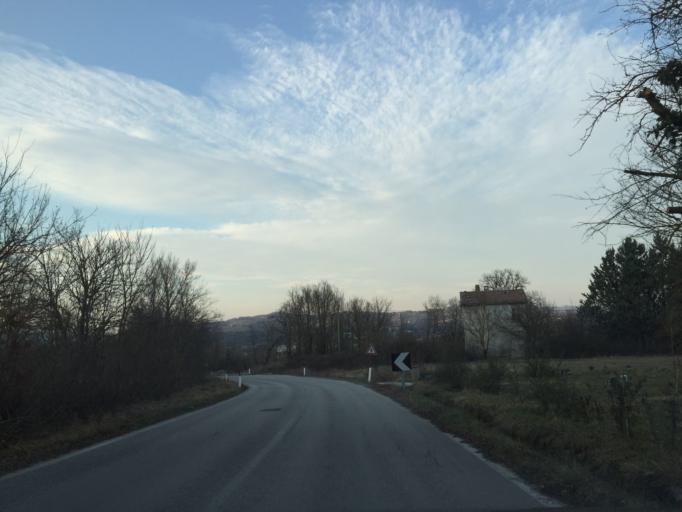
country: IT
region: Molise
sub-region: Provincia di Campobasso
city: Guardiaregia
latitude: 41.4533
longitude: 14.5564
